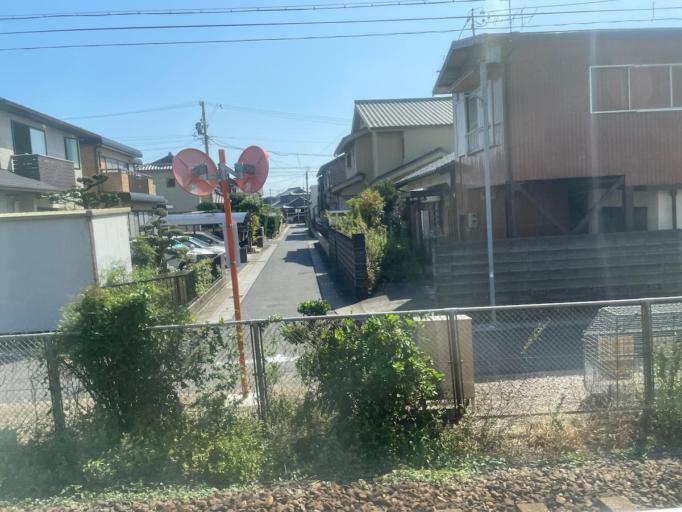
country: JP
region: Mie
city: Kawage
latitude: 34.7963
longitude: 136.5542
